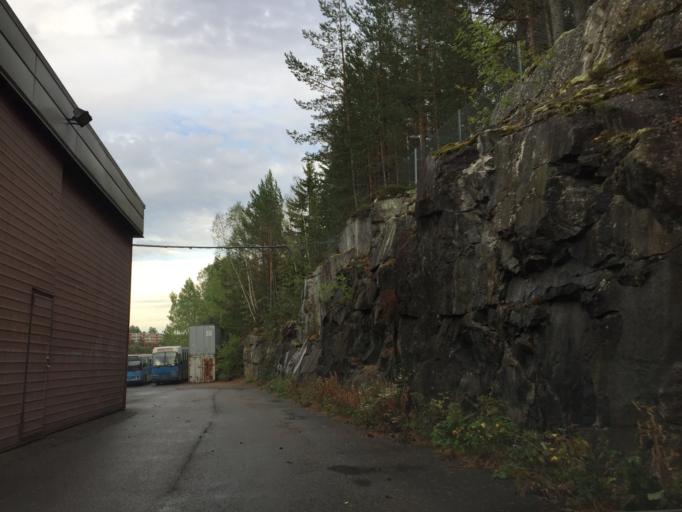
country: NO
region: Akershus
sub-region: Oppegard
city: Kolbotn
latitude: 59.8407
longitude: 10.8195
